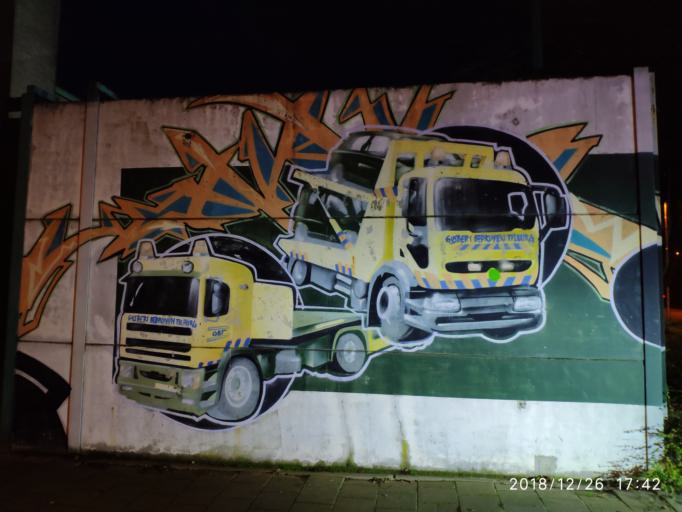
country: NL
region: North Brabant
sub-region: Gemeente Tilburg
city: Tilburg
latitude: 51.5775
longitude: 5.0734
